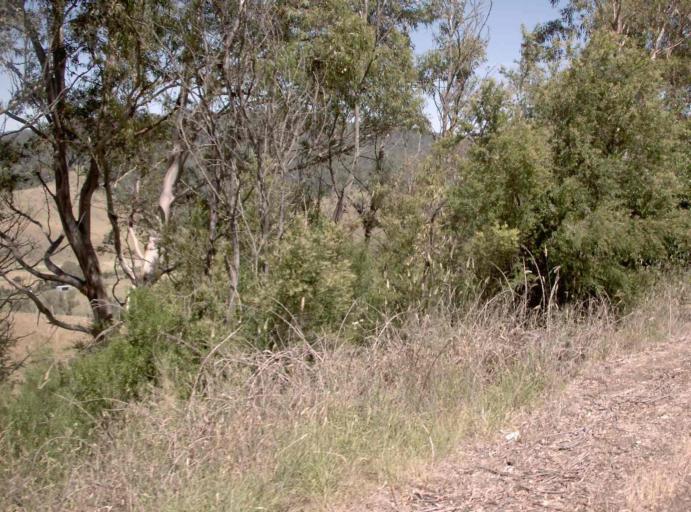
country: AU
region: Victoria
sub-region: East Gippsland
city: Lakes Entrance
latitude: -37.4806
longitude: 148.1830
